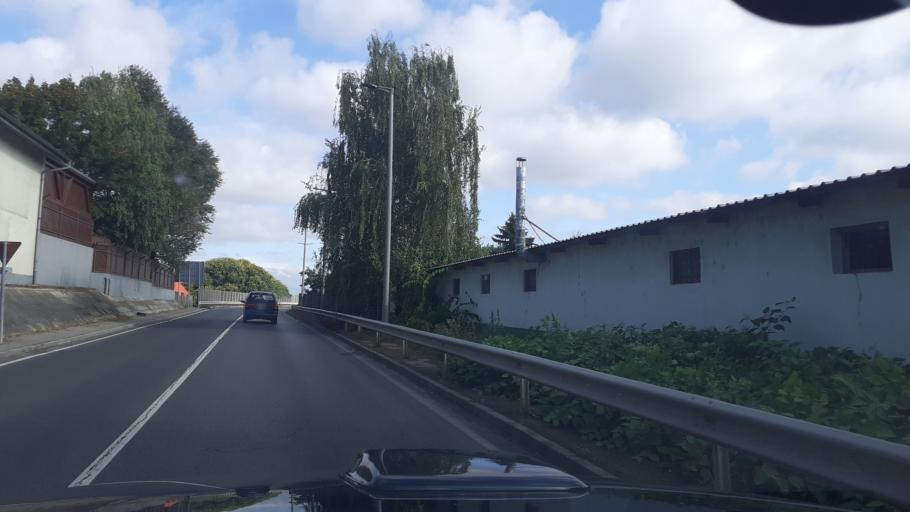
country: HU
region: Tolna
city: Dunafoldvar
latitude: 46.8065
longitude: 18.9293
